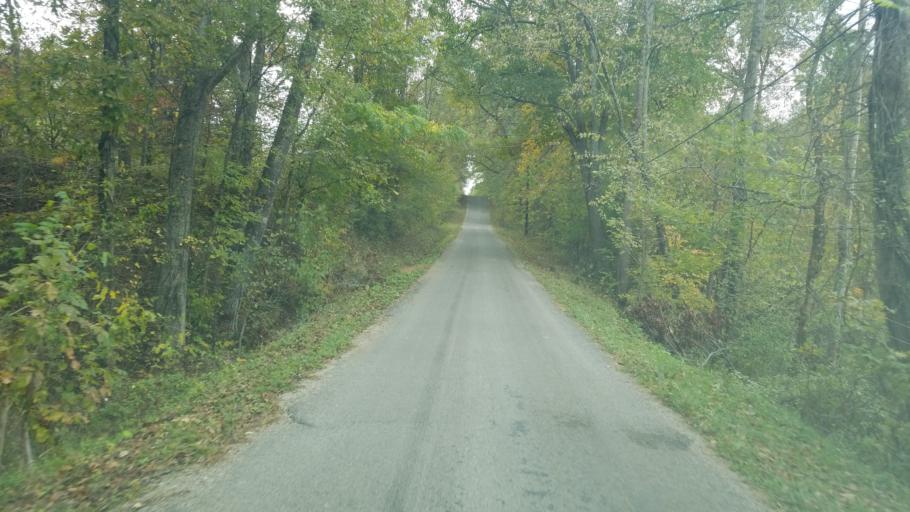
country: US
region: Ohio
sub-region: Jackson County
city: Wellston
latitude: 39.1692
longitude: -82.5664
